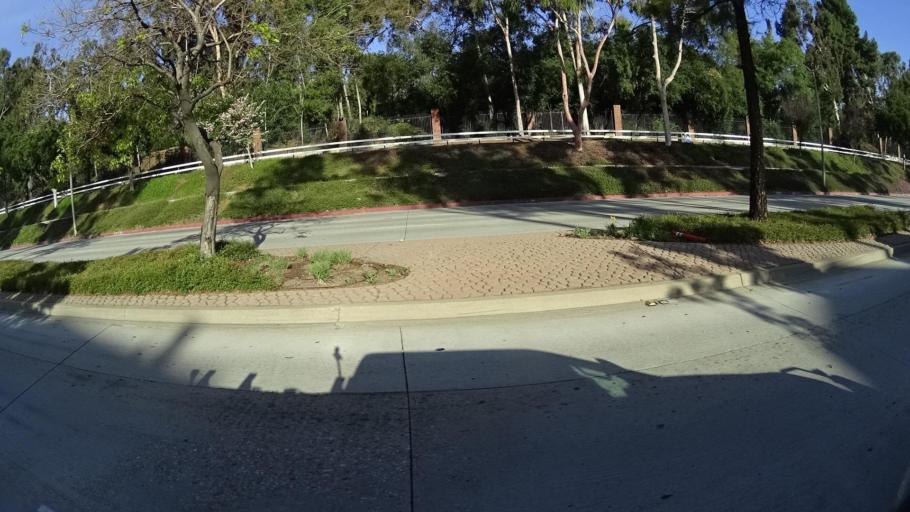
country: US
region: California
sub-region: Los Angeles County
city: South San Jose Hills
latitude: 34.0218
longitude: -117.9187
